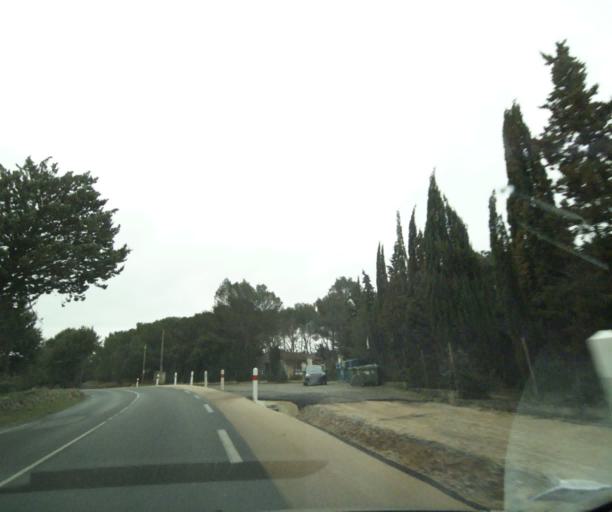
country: FR
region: Provence-Alpes-Cote d'Azur
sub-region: Departement des Bouches-du-Rhone
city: Rognes
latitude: 43.6636
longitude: 5.3318
